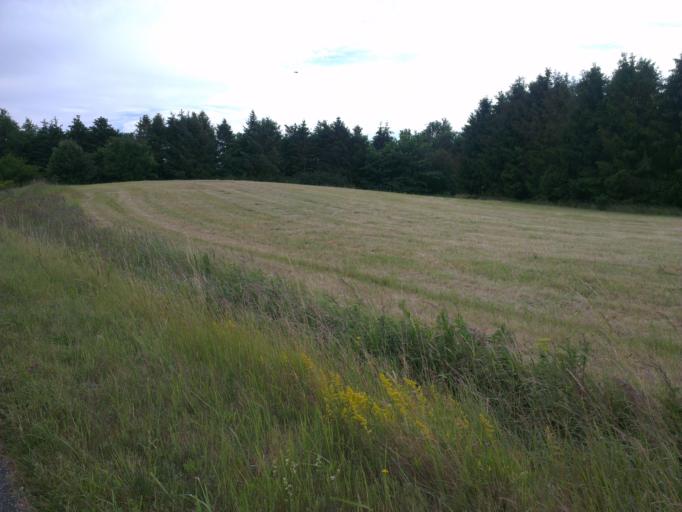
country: DK
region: Capital Region
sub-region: Frederikssund Kommune
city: Jaegerspris
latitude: 55.9019
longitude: 11.9368
